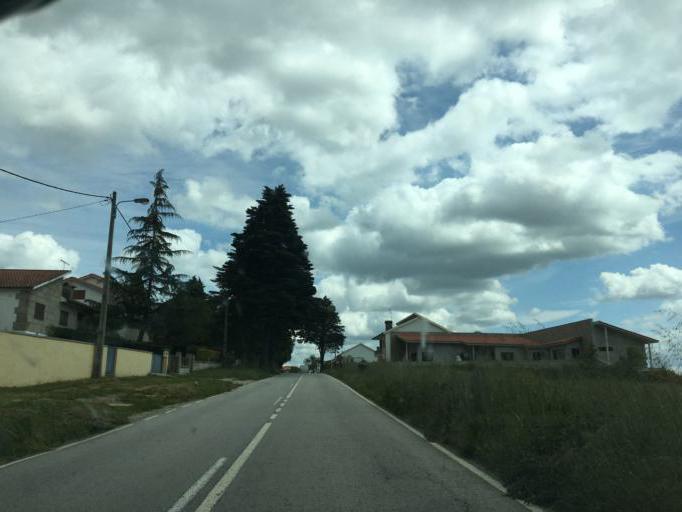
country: PT
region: Vila Real
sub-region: Boticas
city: Boticas
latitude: 41.7031
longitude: -7.6433
